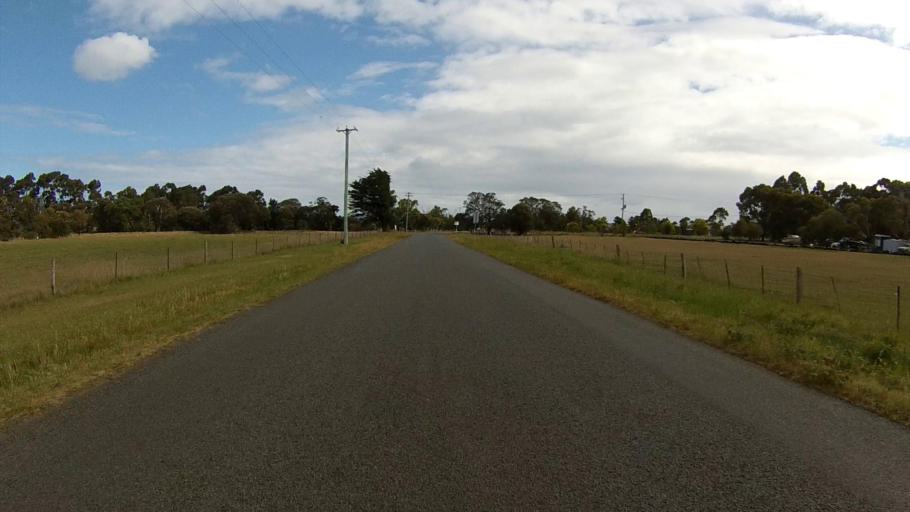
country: AU
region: Tasmania
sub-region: Clarence
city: Acton Park
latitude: -42.8886
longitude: 147.4965
